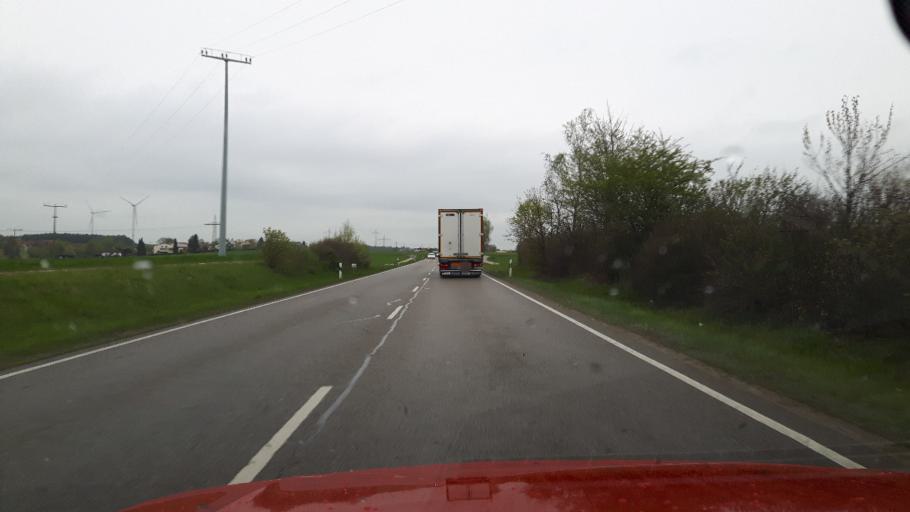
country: DE
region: Bavaria
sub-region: Regierungsbezirk Mittelfranken
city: Burgoberbach
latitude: 49.2447
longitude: 10.6016
